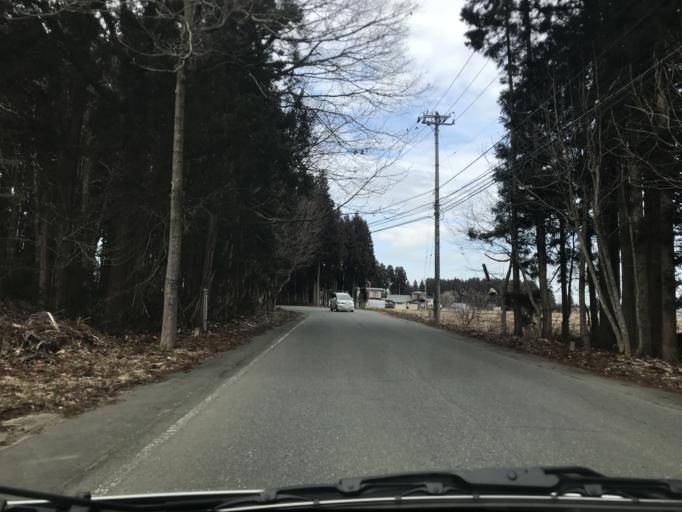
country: JP
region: Iwate
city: Kitakami
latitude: 39.3200
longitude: 140.9864
